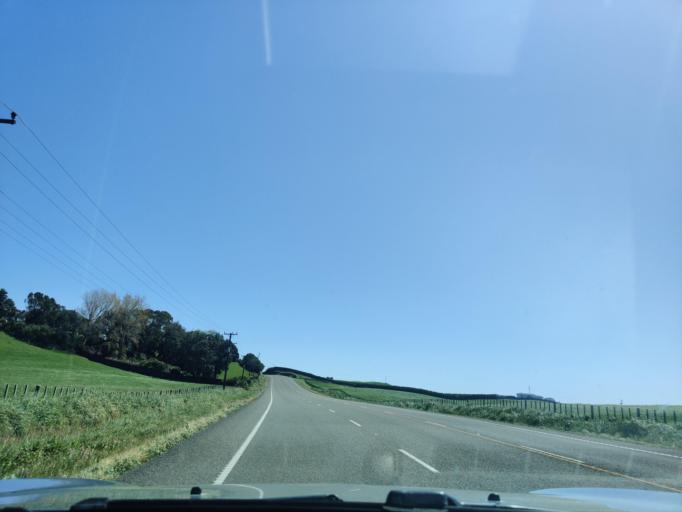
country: NZ
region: Taranaki
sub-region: South Taranaki District
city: Patea
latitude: -39.6825
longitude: 174.4169
